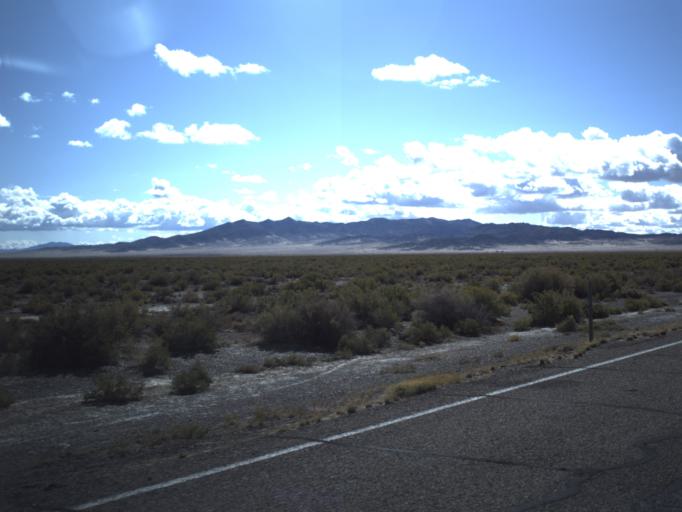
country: US
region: Nevada
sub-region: White Pine County
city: McGill
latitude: 39.0464
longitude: -114.0363
